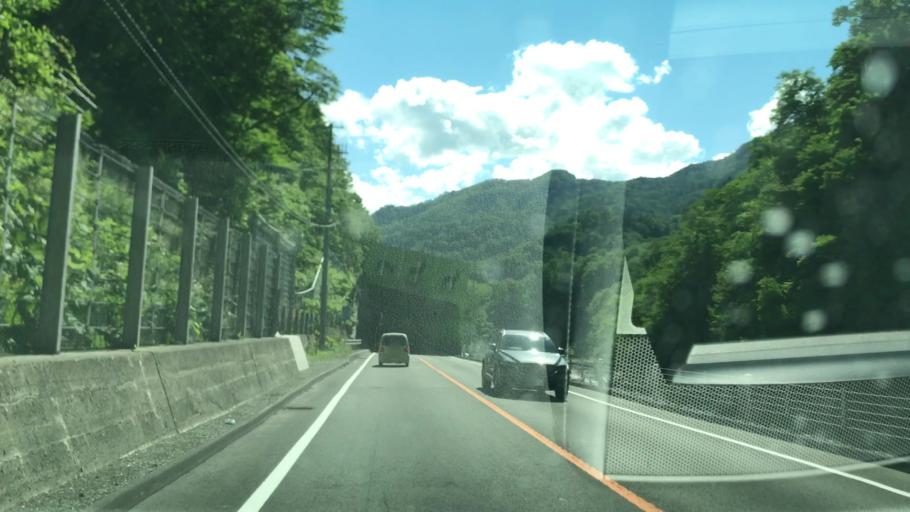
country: JP
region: Hokkaido
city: Shimo-furano
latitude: 42.9389
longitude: 142.5997
